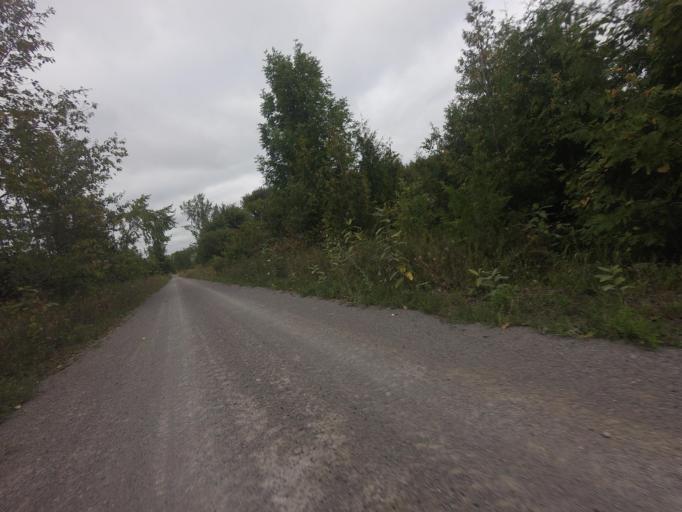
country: CA
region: Ontario
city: Omemee
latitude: 44.4520
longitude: -78.7645
